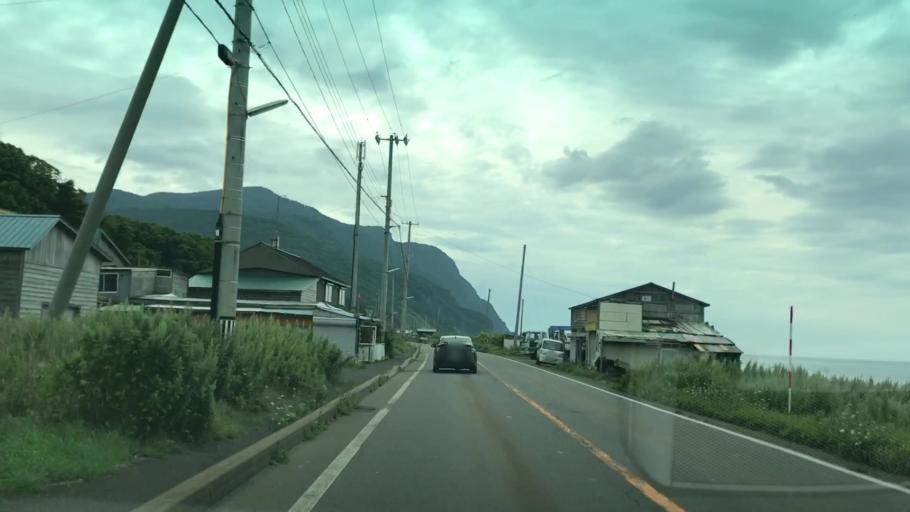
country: JP
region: Hokkaido
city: Iwanai
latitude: 42.9686
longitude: 140.4751
